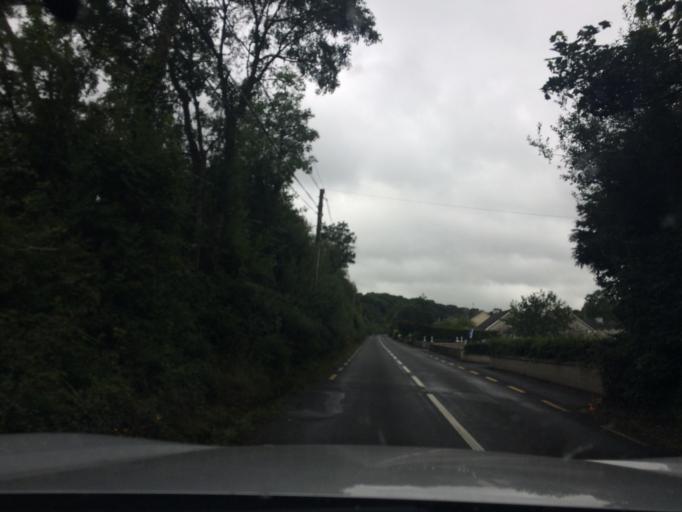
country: IE
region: Munster
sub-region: South Tipperary
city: Cluain Meala
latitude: 52.3352
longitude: -7.7272
